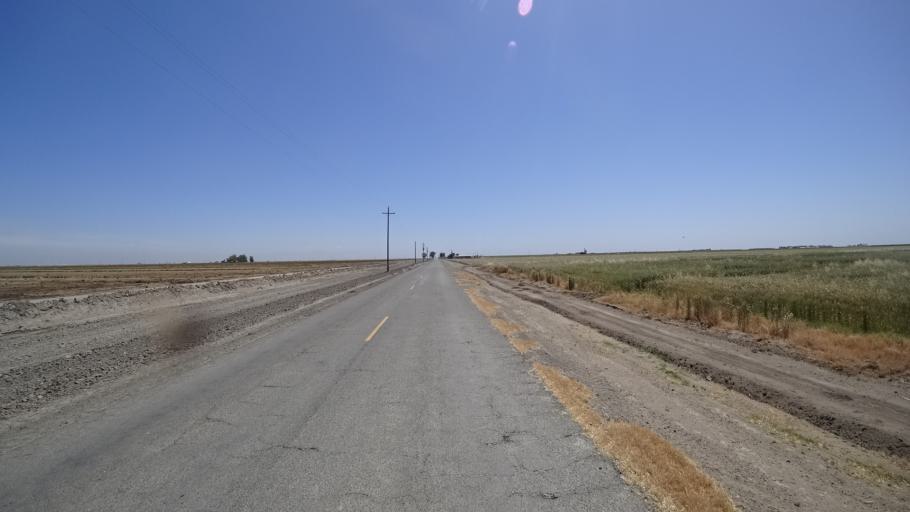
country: US
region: California
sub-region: Kings County
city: Corcoran
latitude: 36.1379
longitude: -119.6591
